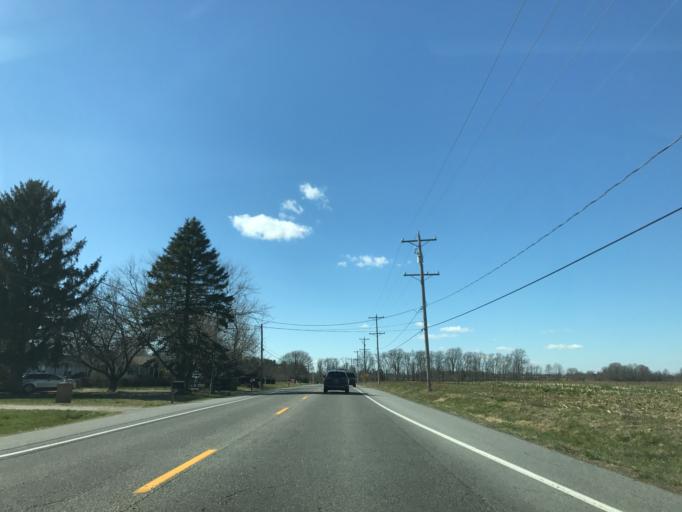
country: US
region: Maryland
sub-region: Kent County
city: Chestertown
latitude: 39.2172
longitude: -76.1267
